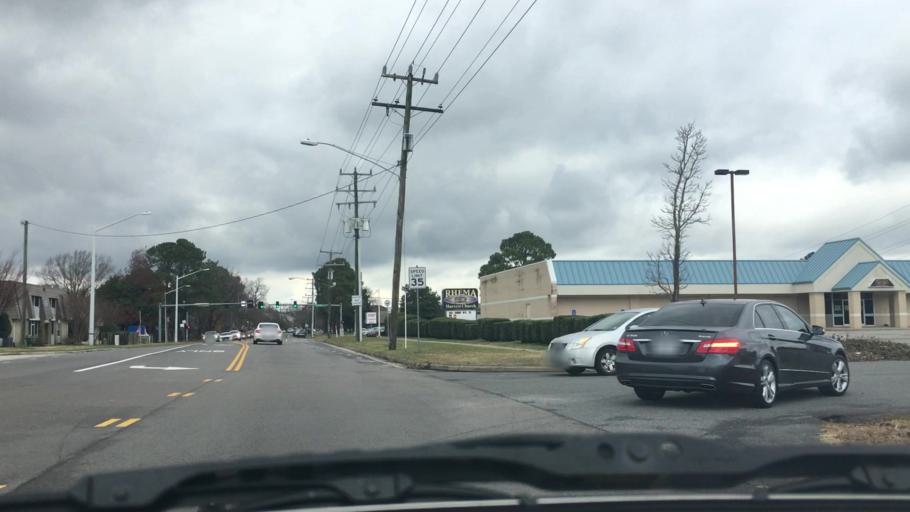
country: US
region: Virginia
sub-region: City of Chesapeake
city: Chesapeake
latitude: 36.8603
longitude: -76.1757
